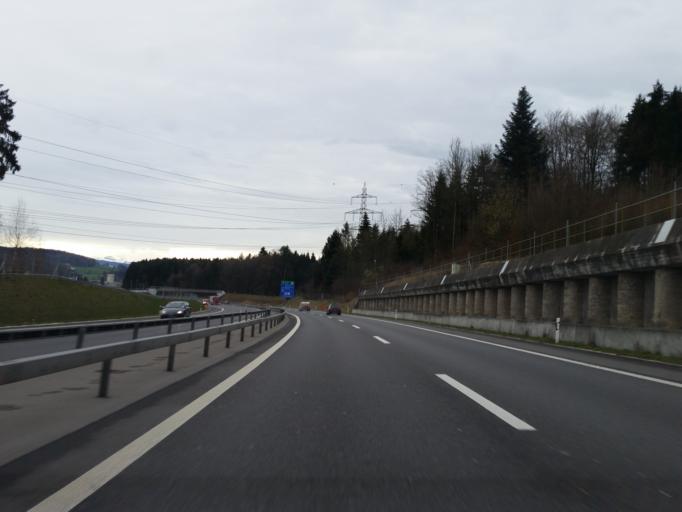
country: CH
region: Zurich
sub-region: Bezirk Affoltern
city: Obfelden / Toussen
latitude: 47.2797
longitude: 8.4277
